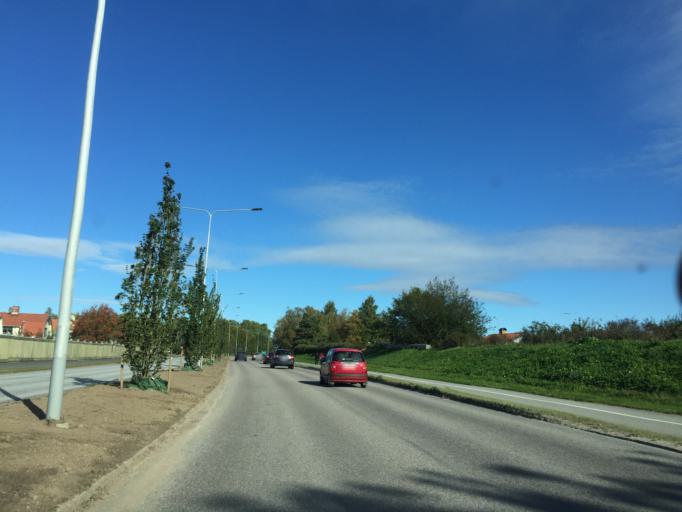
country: SE
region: OErebro
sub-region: Orebro Kommun
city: Orebro
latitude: 59.2912
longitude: 15.2255
